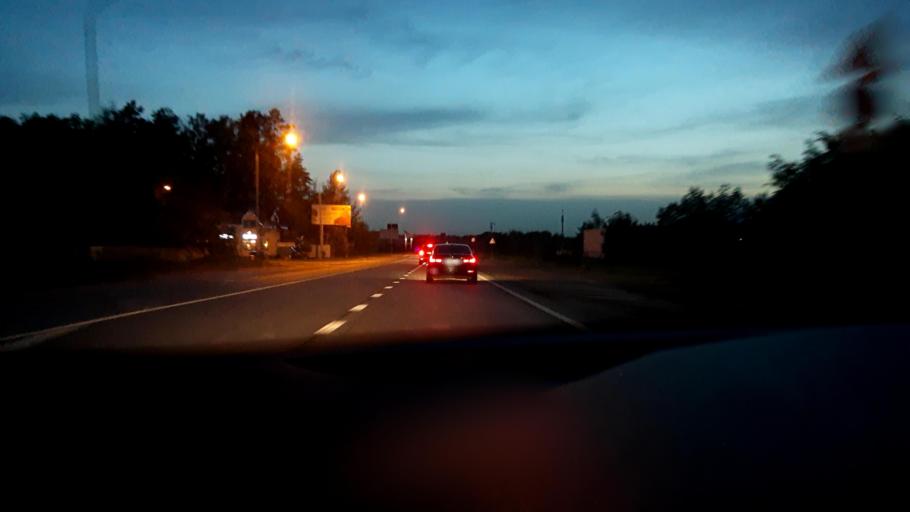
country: RU
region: Moskovskaya
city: Opalikha
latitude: 55.7858
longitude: 37.2293
